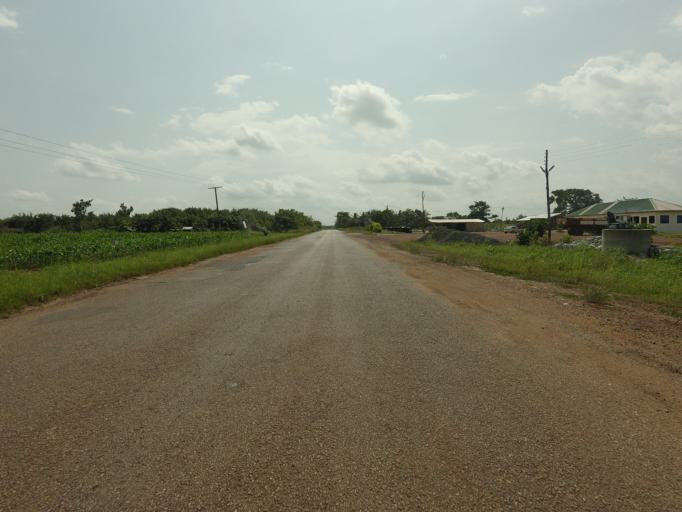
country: TG
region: Maritime
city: Lome
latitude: 6.2553
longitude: 0.9664
